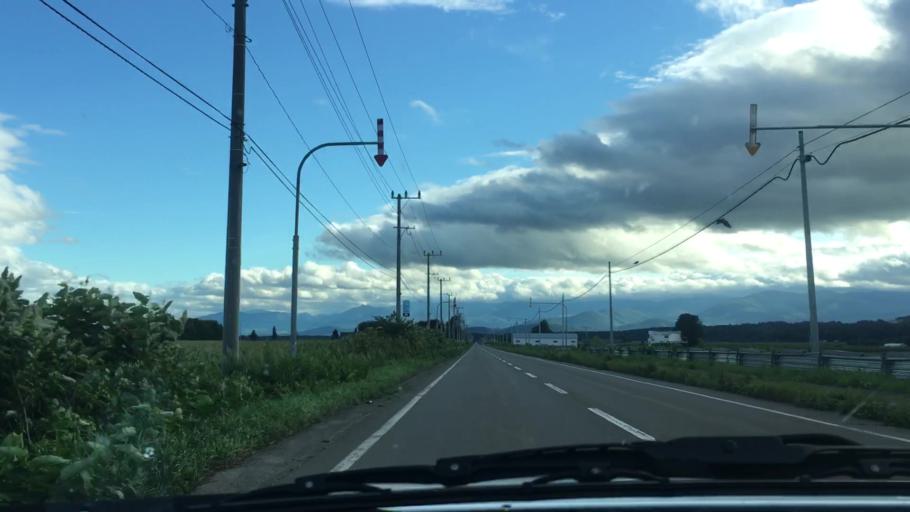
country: JP
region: Hokkaido
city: Otofuke
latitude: 43.1575
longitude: 142.9029
